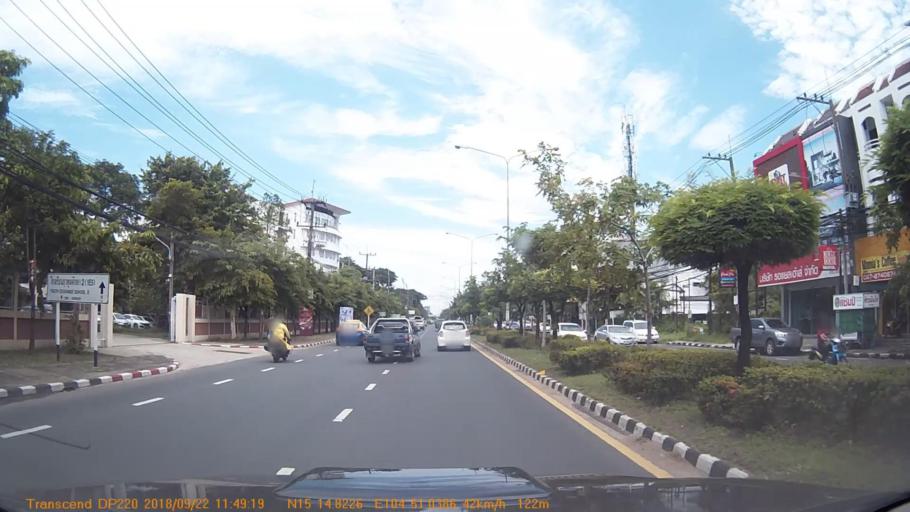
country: TH
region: Changwat Ubon Ratchathani
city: Ubon Ratchathani
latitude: 15.2468
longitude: 104.8507
